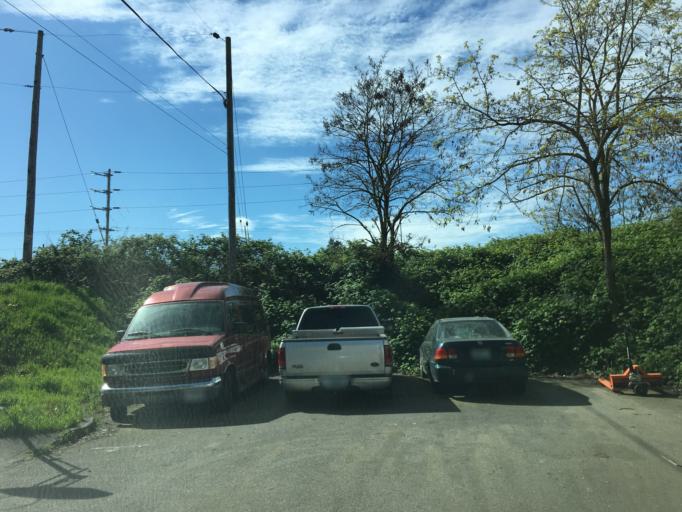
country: US
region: Oregon
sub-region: Multnomah County
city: Lents
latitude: 45.5342
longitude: -122.5934
